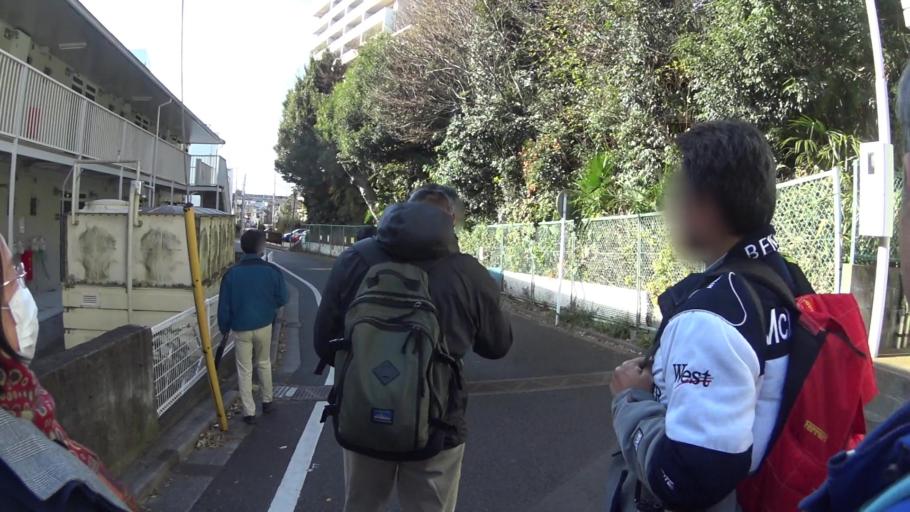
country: JP
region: Saitama
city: Yono
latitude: 35.8522
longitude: 139.6439
